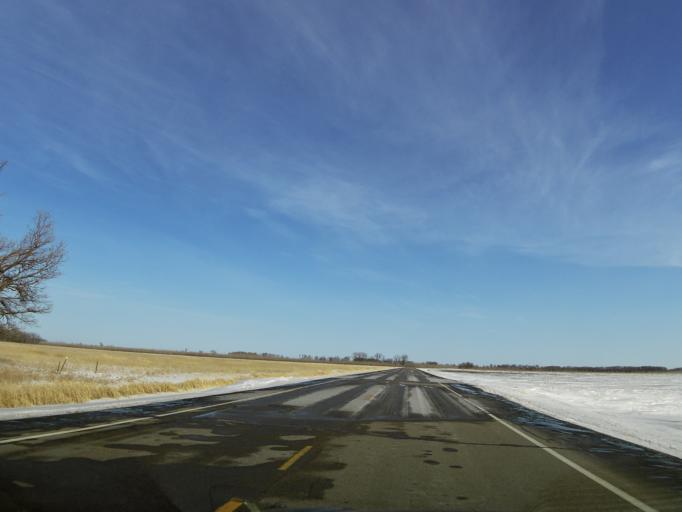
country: US
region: North Dakota
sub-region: Walsh County
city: Grafton
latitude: 48.4135
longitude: -97.1240
